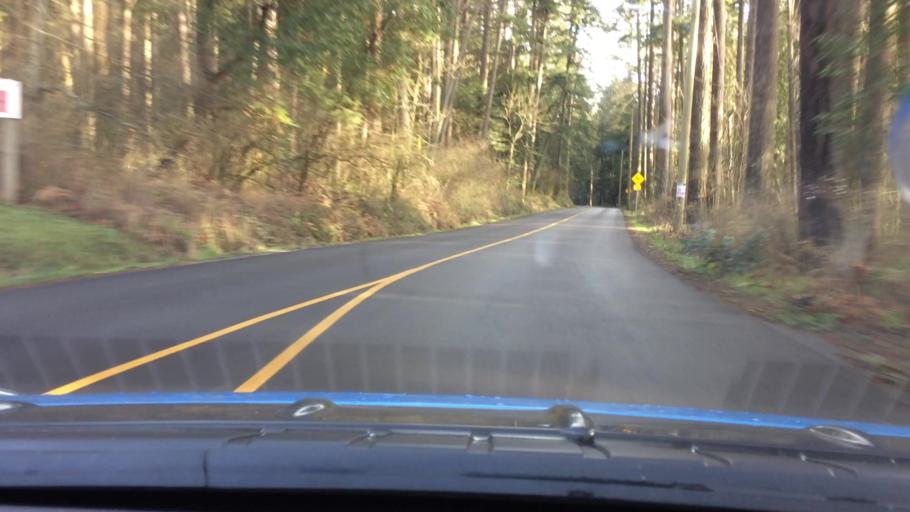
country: CA
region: British Columbia
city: Oak Bay
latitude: 48.4908
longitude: -123.3378
